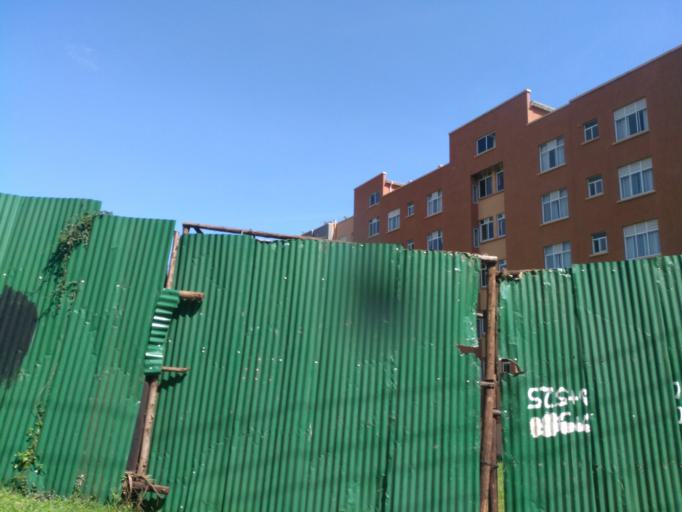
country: UG
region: Central Region
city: Kampala Central Division
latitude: 0.3242
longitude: 32.5825
